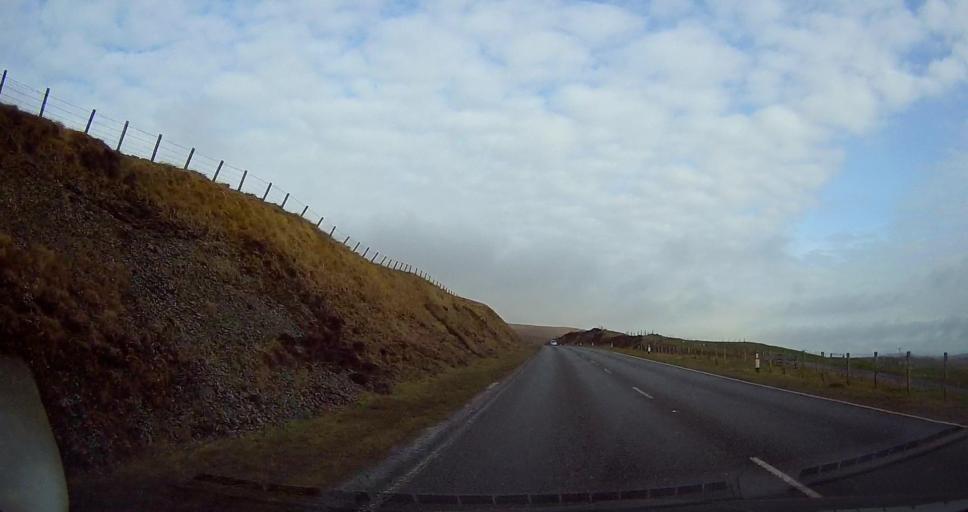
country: GB
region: Scotland
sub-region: Shetland Islands
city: Sandwick
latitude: 60.0653
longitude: -1.2230
